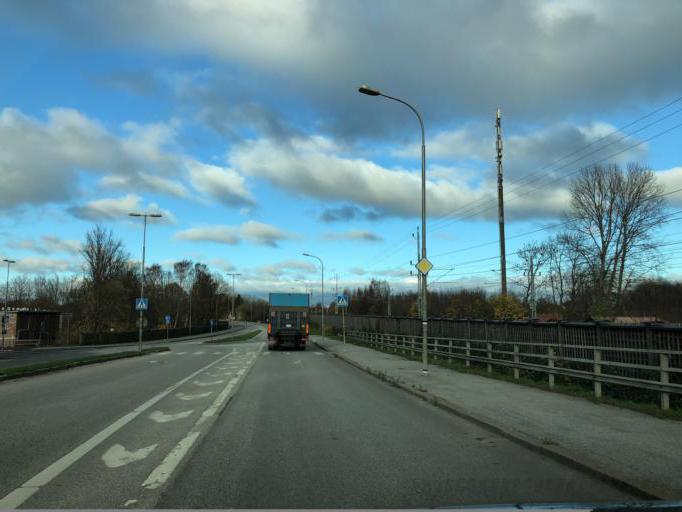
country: SE
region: Skane
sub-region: Lunds Kommun
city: Lund
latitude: 55.7217
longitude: 13.1834
